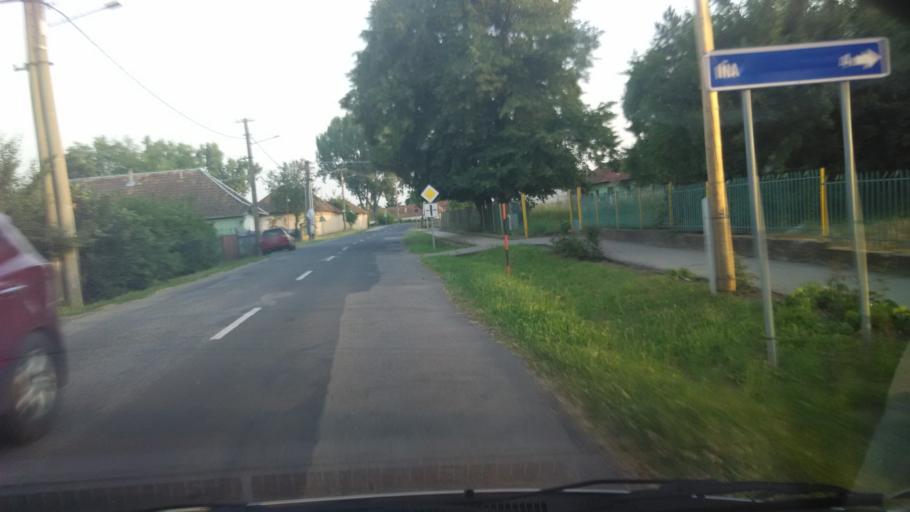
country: SK
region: Nitriansky
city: Tlmace
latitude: 48.1824
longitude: 18.4547
